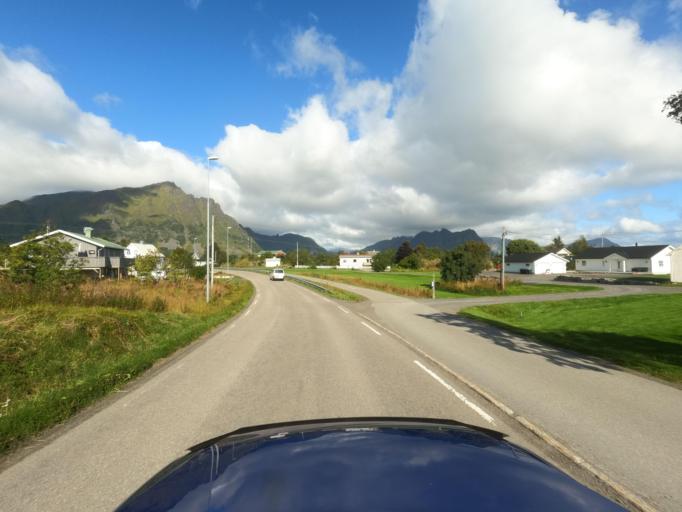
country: NO
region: Nordland
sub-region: Vestvagoy
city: Evjen
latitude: 68.1490
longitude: 13.8438
